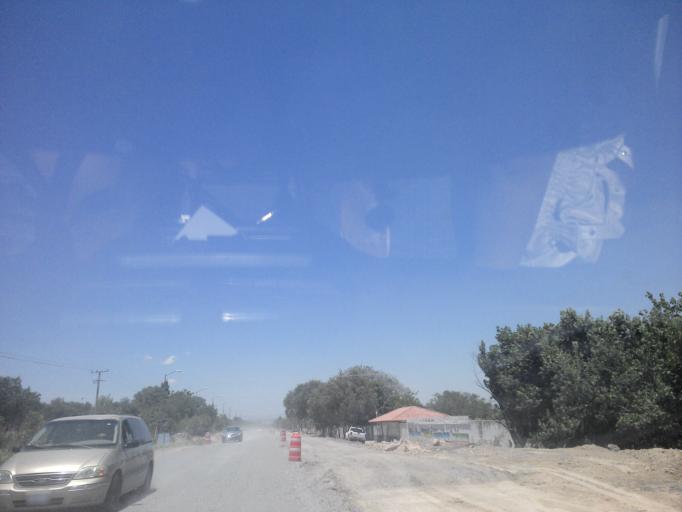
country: MX
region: Guanajuato
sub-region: San Francisco del Rincon
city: San Ignacio de Hidalgo
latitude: 20.9399
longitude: -101.9110
